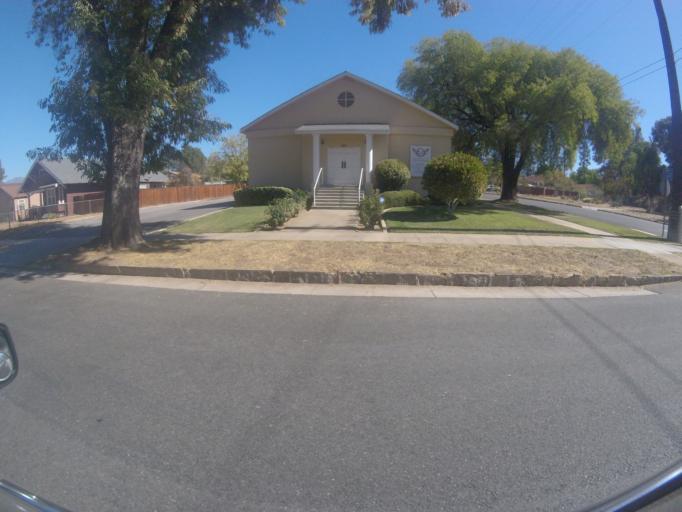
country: US
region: California
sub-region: San Bernardino County
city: Redlands
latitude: 34.0606
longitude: -117.1738
